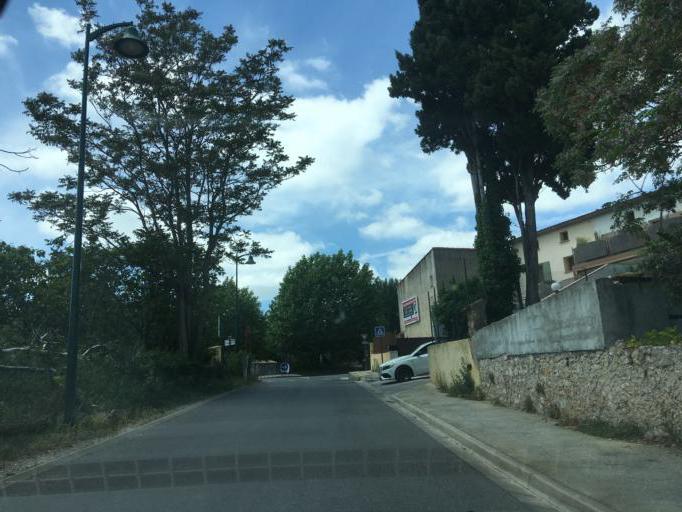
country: FR
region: Provence-Alpes-Cote d'Azur
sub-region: Departement du Var
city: Flayosc
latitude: 43.5326
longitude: 6.3988
